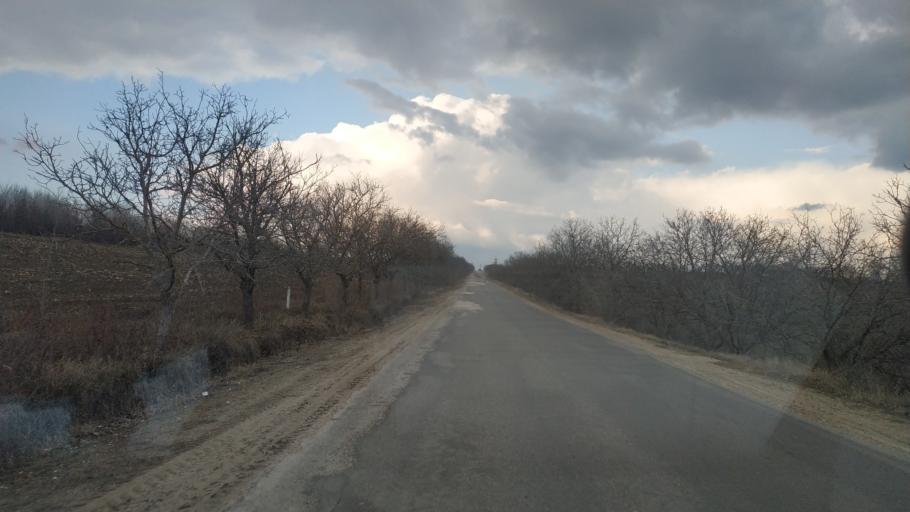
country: MD
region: Anenii Noi
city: Anenii Noi
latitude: 46.9537
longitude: 29.2827
